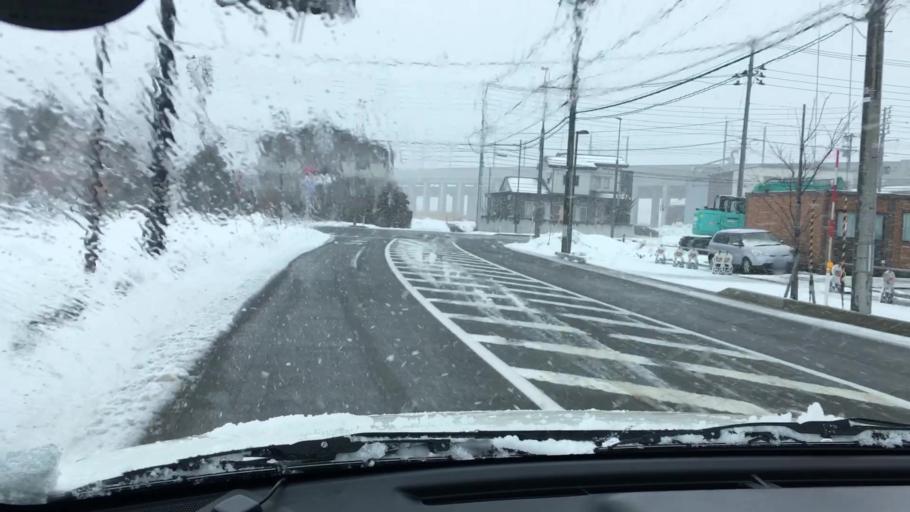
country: JP
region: Niigata
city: Joetsu
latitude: 37.0824
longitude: 138.2449
